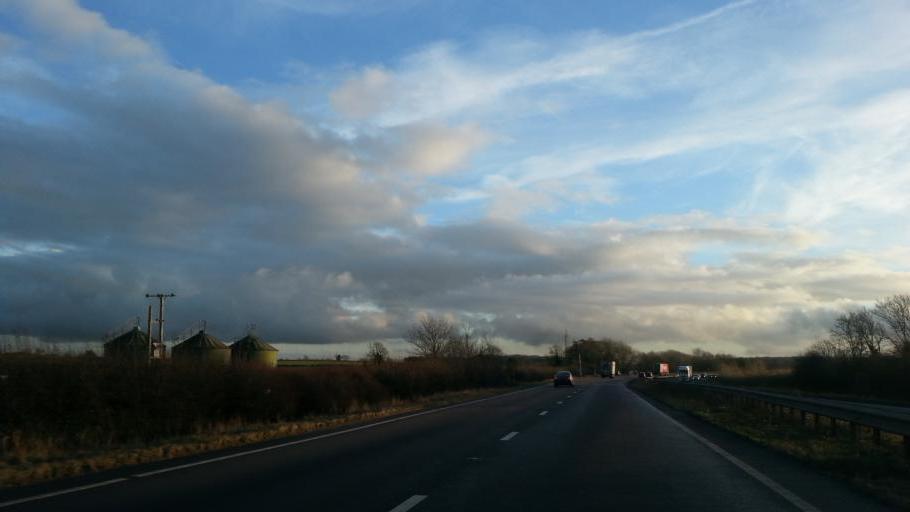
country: GB
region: England
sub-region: Northamptonshire
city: Brackley
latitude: 52.0064
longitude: -1.1591
